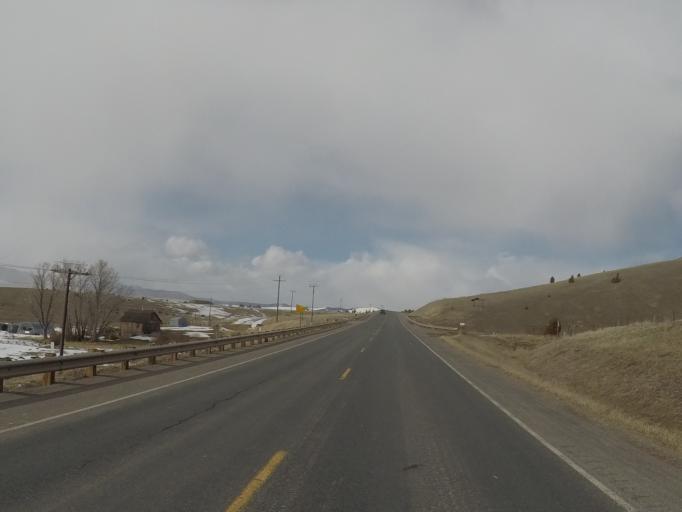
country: US
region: Montana
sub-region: Granite County
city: Philipsburg
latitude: 46.2865
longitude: -113.3227
